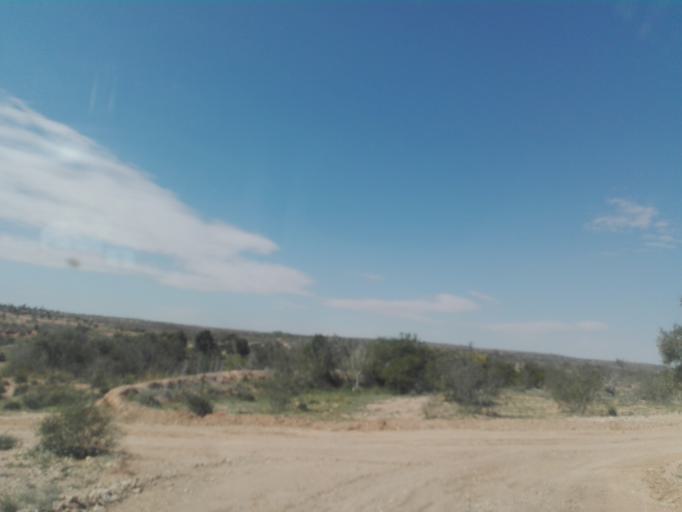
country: TN
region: Safaqis
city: Sfax
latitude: 34.6962
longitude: 10.5309
